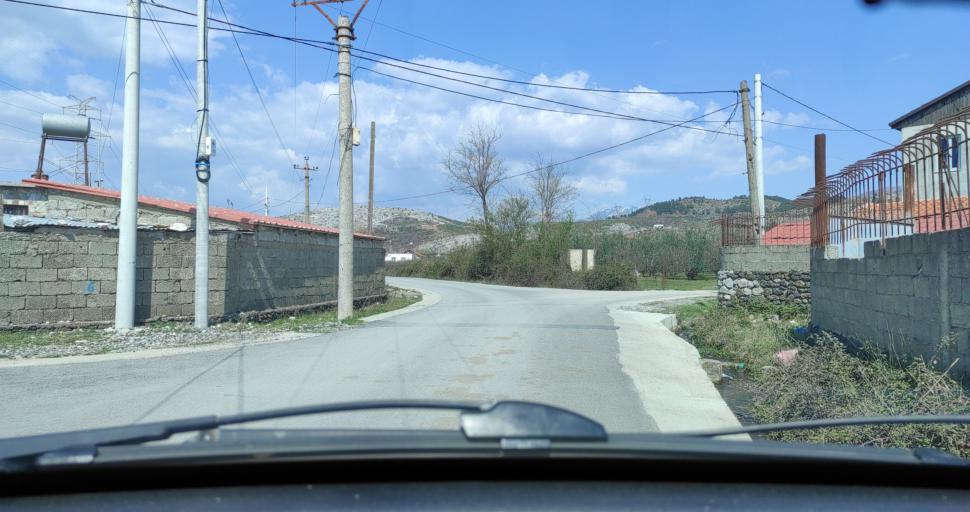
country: AL
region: Shkoder
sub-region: Rrethi i Shkodres
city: Vau i Dejes
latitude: 42.0037
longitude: 19.6420
